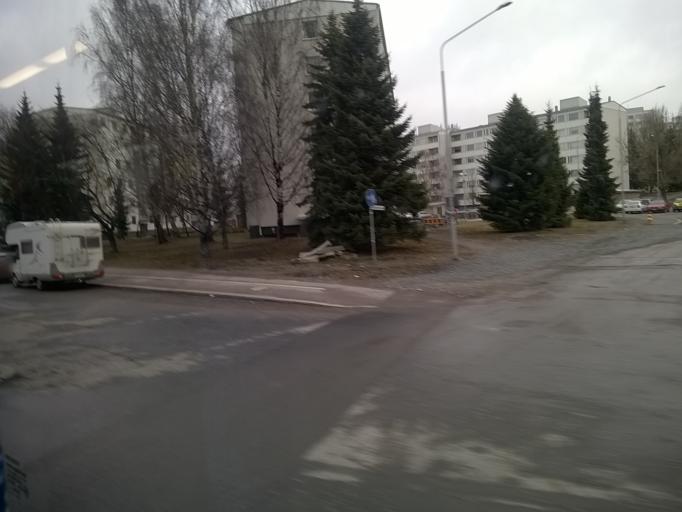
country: FI
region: Pirkanmaa
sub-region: Tampere
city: Tampere
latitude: 61.4945
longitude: 23.8137
